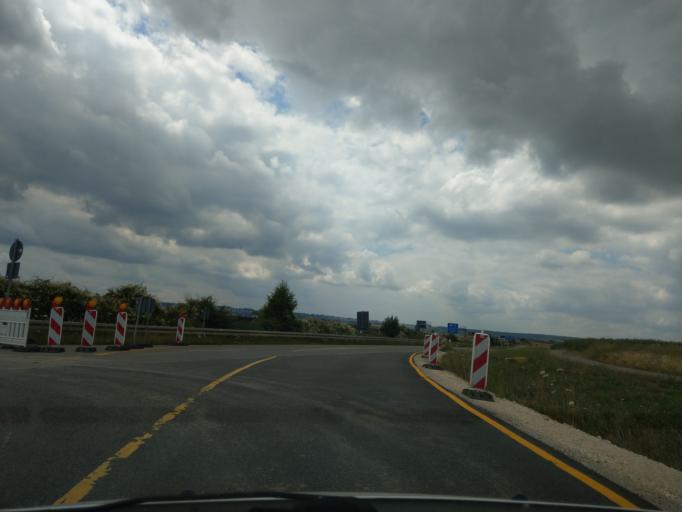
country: DE
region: Baden-Wuerttemberg
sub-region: Regierungsbezirk Stuttgart
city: Ostfildern
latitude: 48.6975
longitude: 9.2422
